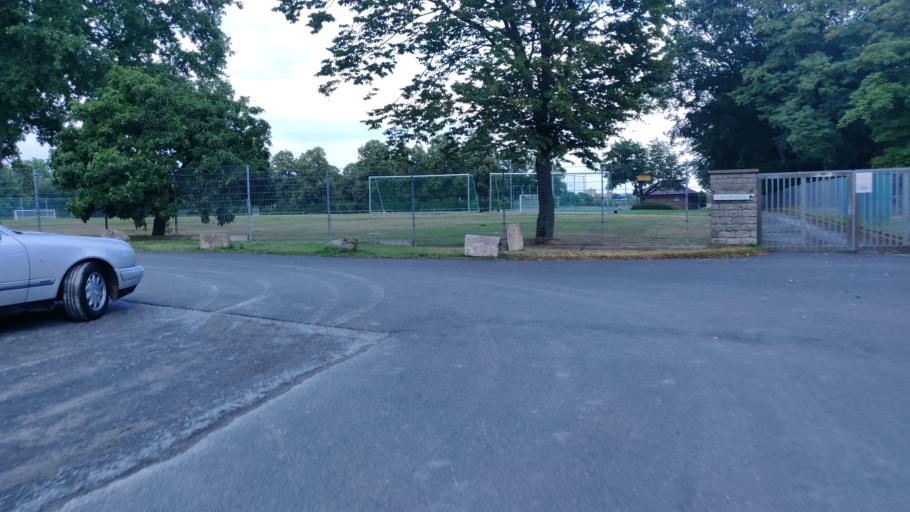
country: DE
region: Bavaria
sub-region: Regierungsbezirk Unterfranken
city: Niederwerrn
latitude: 50.0530
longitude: 10.1970
